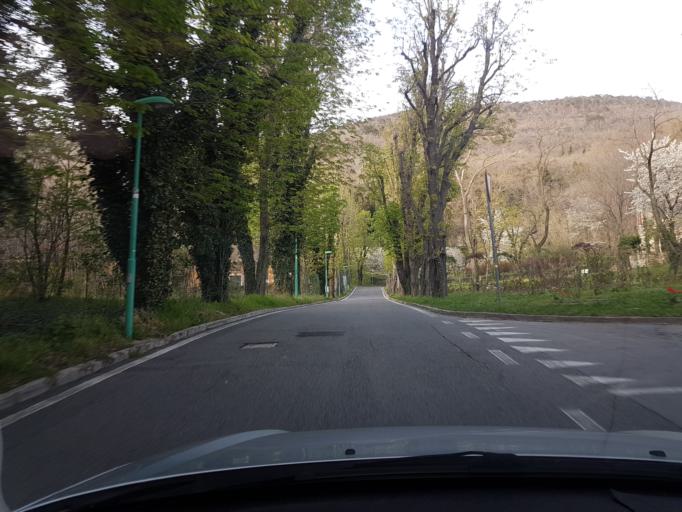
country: IT
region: Friuli Venezia Giulia
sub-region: Provincia di Trieste
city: Trieste
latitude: 45.6614
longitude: 13.8031
